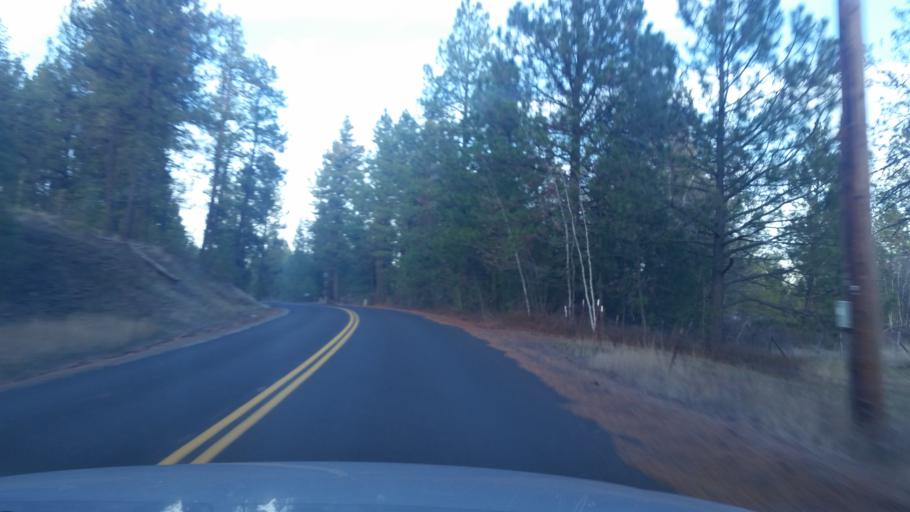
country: US
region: Washington
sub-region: Spokane County
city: Cheney
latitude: 47.5014
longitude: -117.4744
